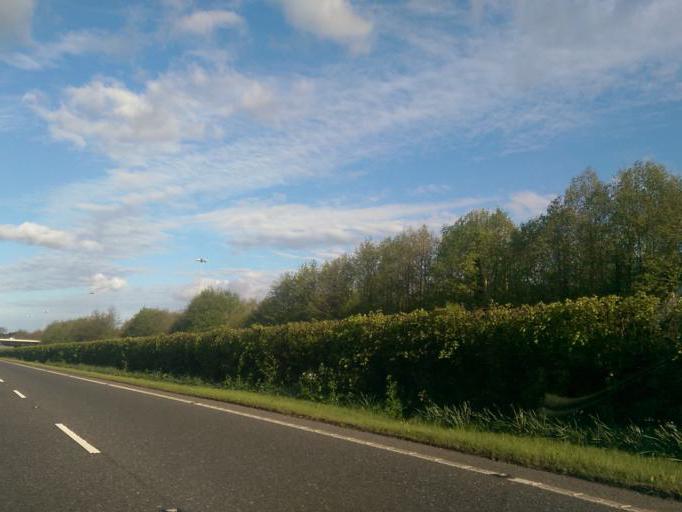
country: IE
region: Leinster
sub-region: Kildare
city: Leixlip
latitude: 53.3583
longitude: -6.4797
